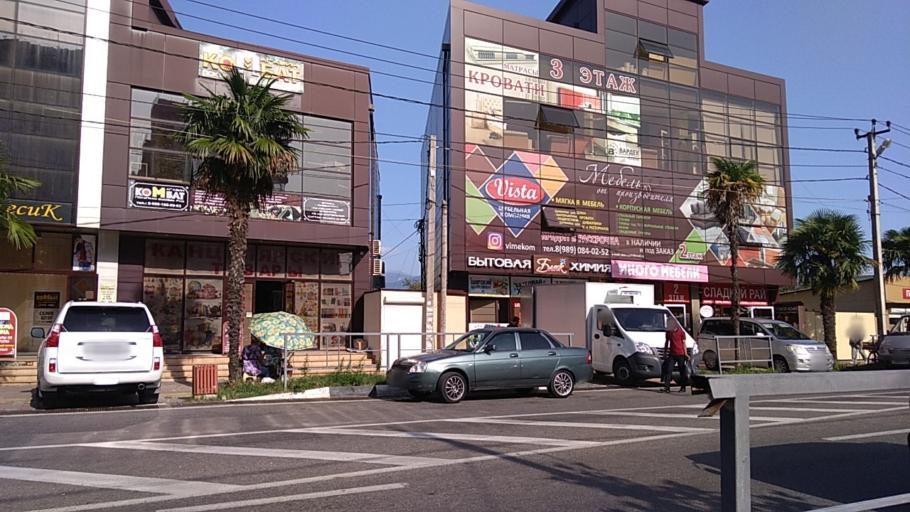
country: RU
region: Krasnodarskiy
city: Vysokoye
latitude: 43.4005
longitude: 40.0026
